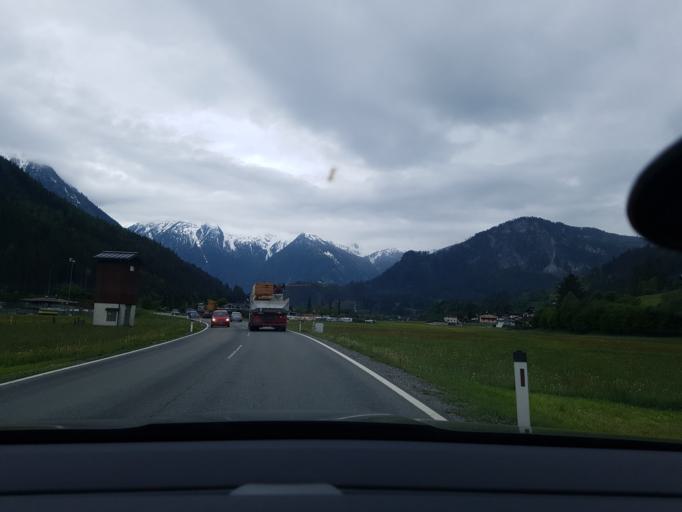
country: AT
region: Salzburg
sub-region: Politischer Bezirk Zell am See
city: Wald im Pinzgau
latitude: 47.2450
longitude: 12.2143
